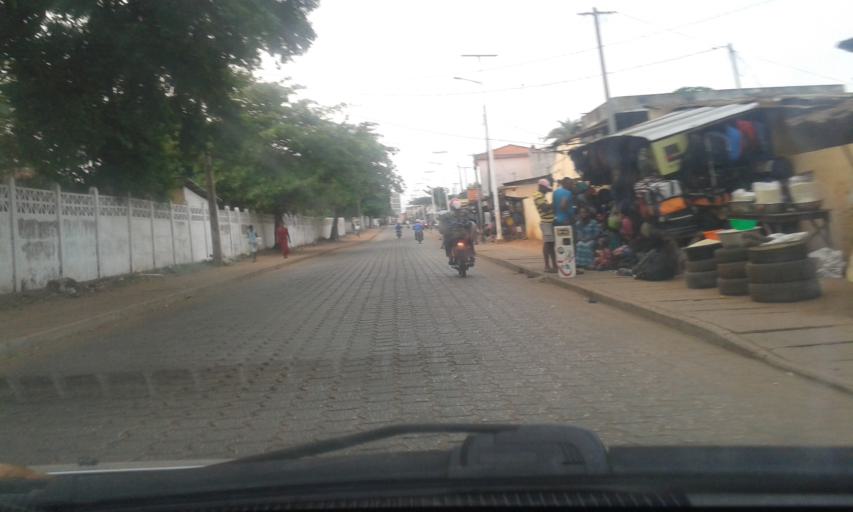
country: BJ
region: Queme
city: Porto-Novo
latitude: 6.4799
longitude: 2.6204
